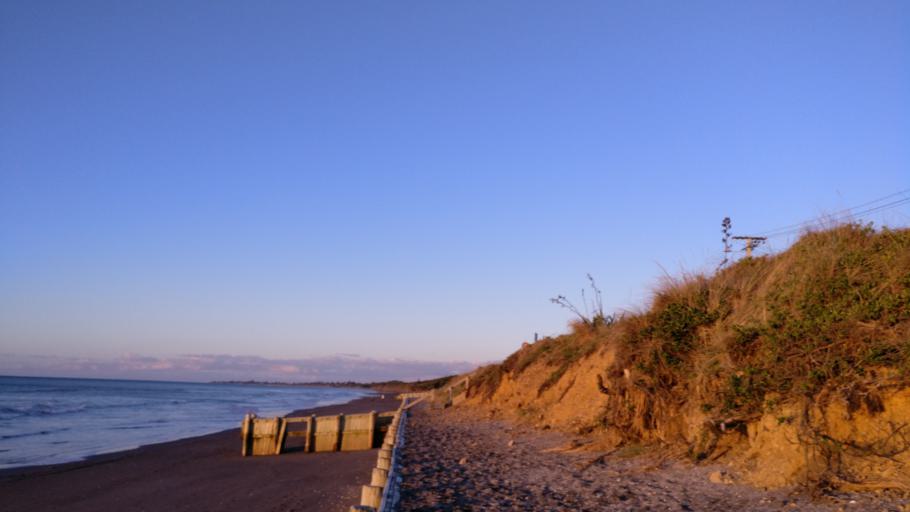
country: NZ
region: Wellington
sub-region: Kapiti Coast District
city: Paraparaumu
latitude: -40.9777
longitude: 174.9566
